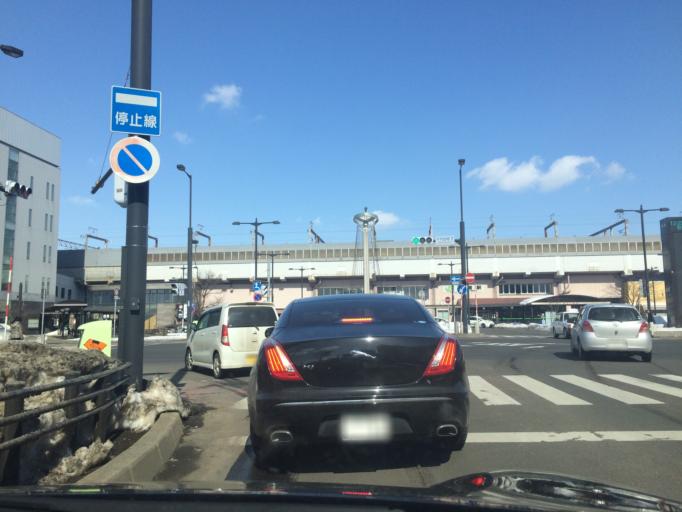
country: JP
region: Hokkaido
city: Chitose
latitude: 42.8276
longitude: 141.6508
